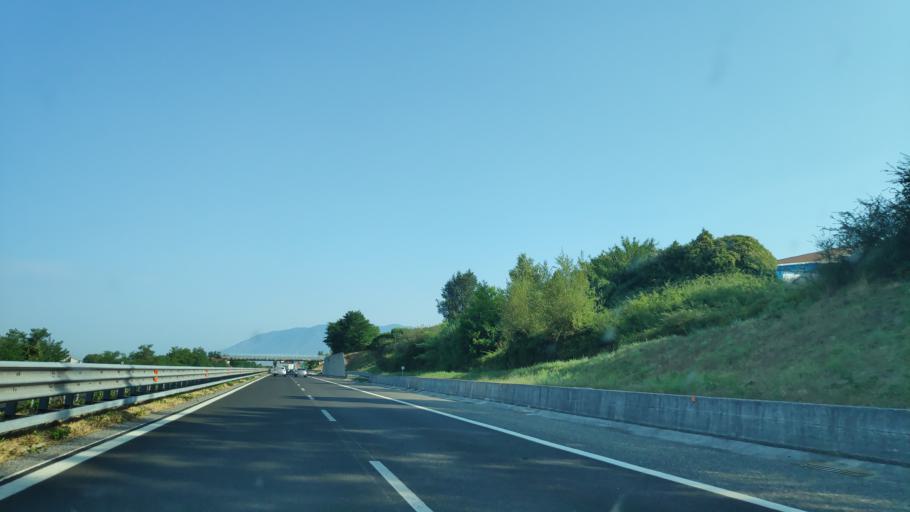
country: IT
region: Campania
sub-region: Provincia di Salerno
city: Buonabitacolo
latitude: 40.2787
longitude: 15.6536
